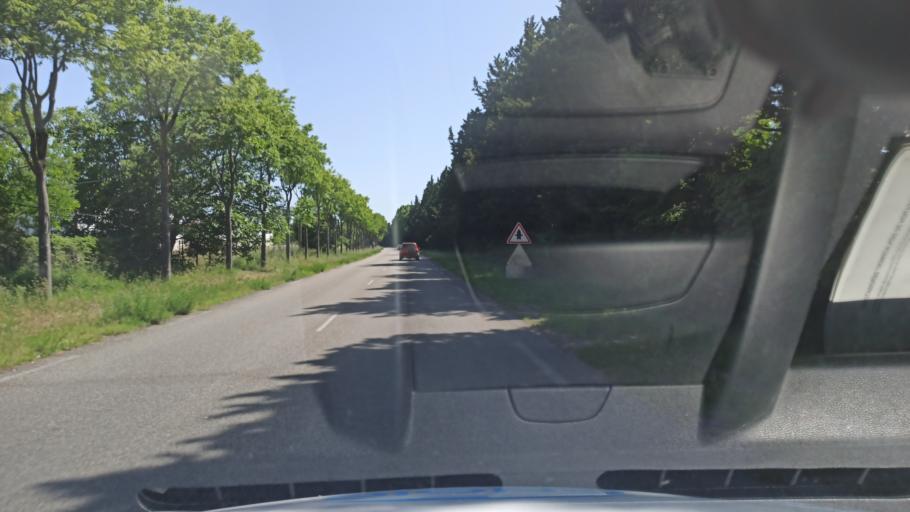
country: FR
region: Provence-Alpes-Cote d'Azur
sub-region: Departement des Bouches-du-Rhone
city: Saint-Andiol
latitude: 43.8420
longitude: 4.9243
